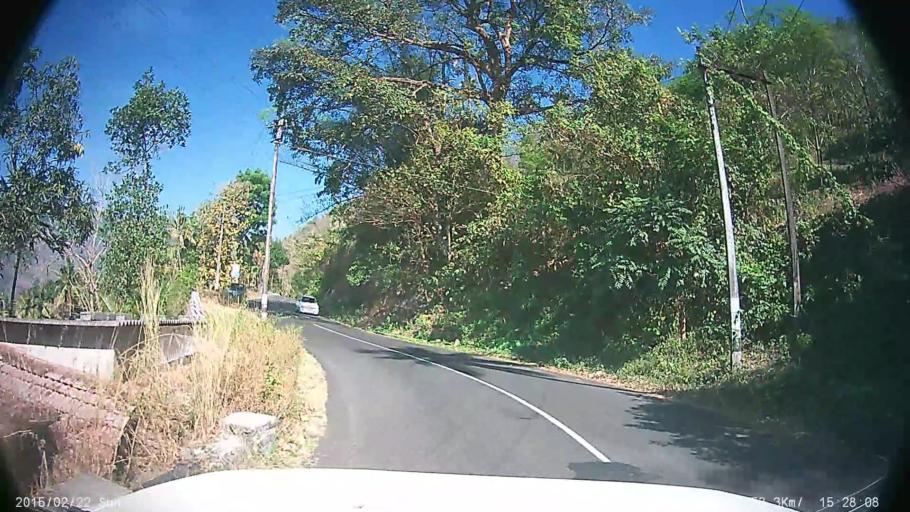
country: IN
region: Kerala
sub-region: Kottayam
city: Erattupetta
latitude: 9.5564
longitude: 76.9396
